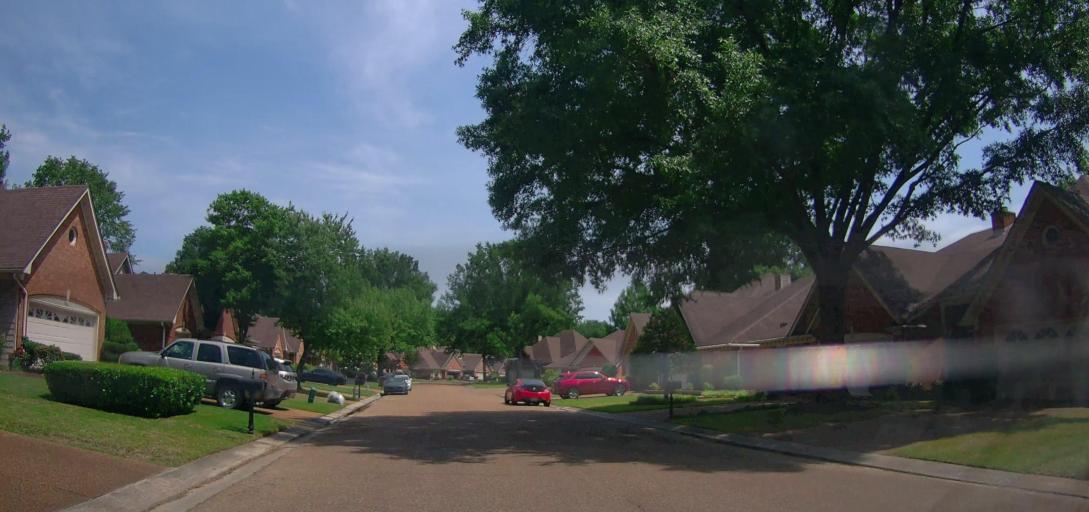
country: US
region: Tennessee
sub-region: Shelby County
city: Germantown
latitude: 35.0408
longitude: -89.7856
